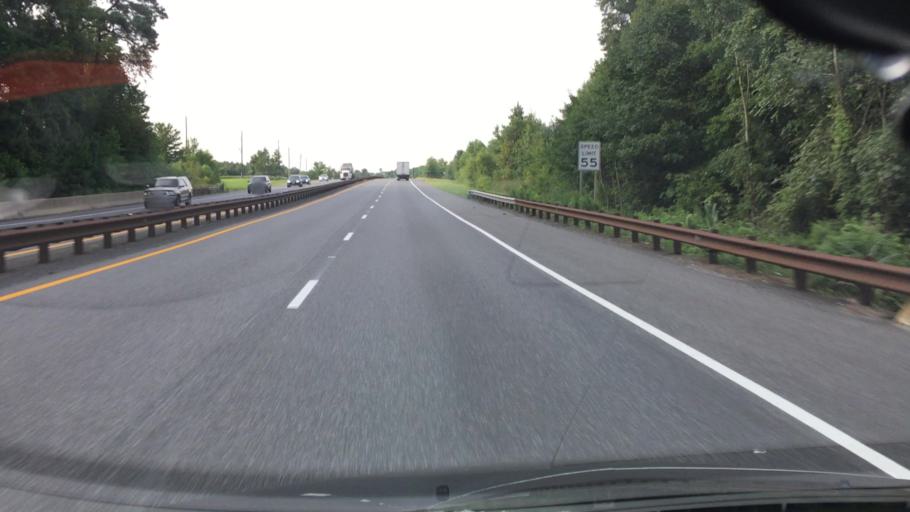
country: US
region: Delaware
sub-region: Sussex County
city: Selbyville
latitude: 38.4094
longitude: -75.2127
